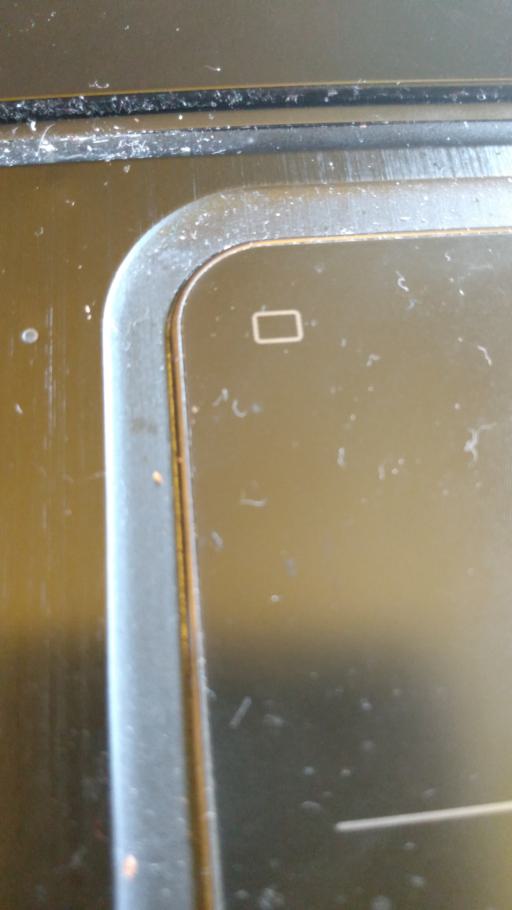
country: RU
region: Moskovskaya
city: Kolomna
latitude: 55.0518
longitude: 38.8971
